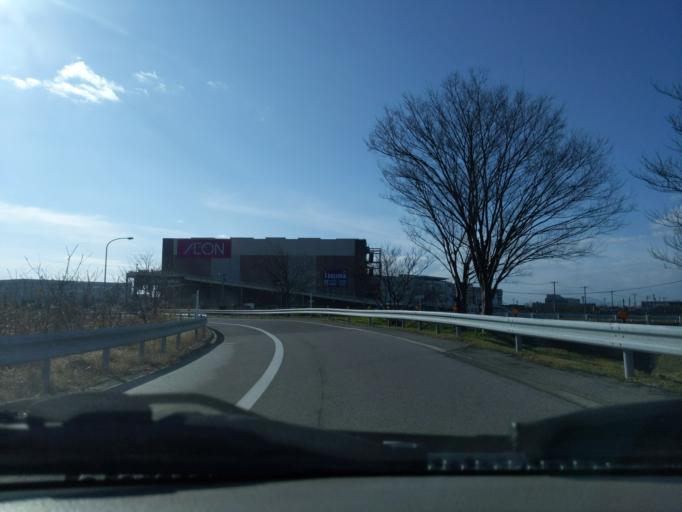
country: JP
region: Niigata
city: Kameda-honcho
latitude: 37.8788
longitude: 139.0836
